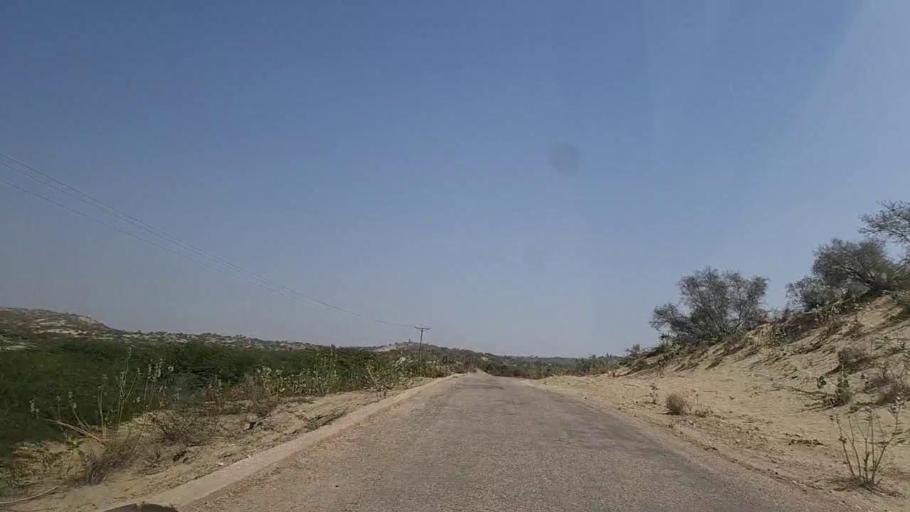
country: PK
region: Sindh
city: Diplo
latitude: 24.5146
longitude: 69.3721
